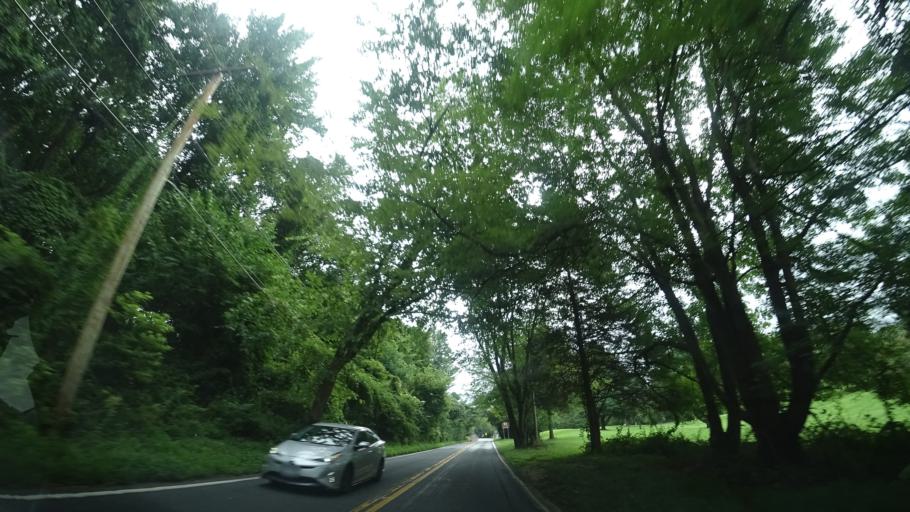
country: US
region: Virginia
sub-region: Loudoun County
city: Lowes Island
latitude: 39.0789
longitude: -77.3299
